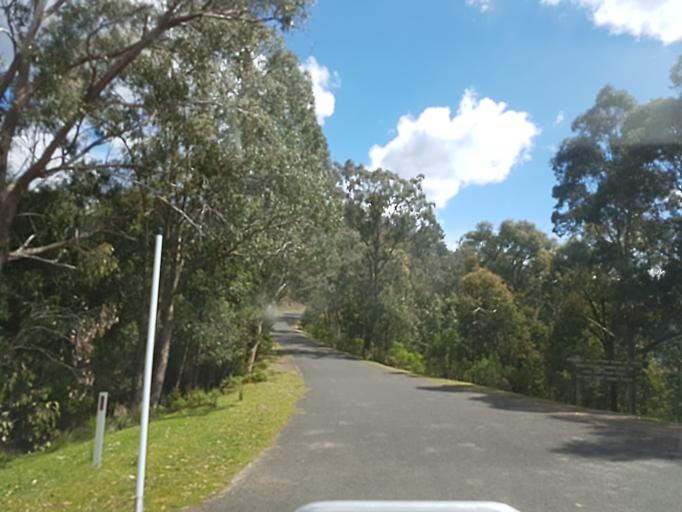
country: AU
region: Victoria
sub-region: East Gippsland
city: Bairnsdale
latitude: -37.4087
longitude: 147.2499
